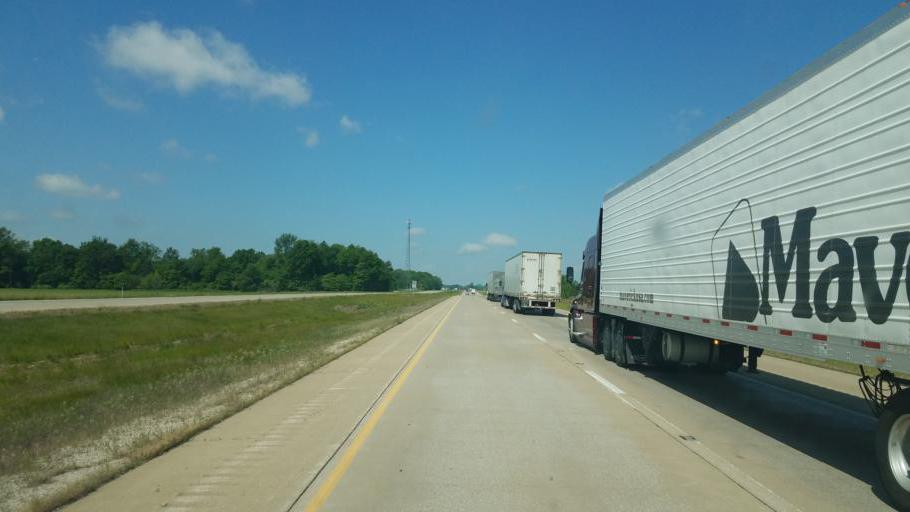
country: US
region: Illinois
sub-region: Clark County
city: Marshall
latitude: 39.4256
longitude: -87.6020
